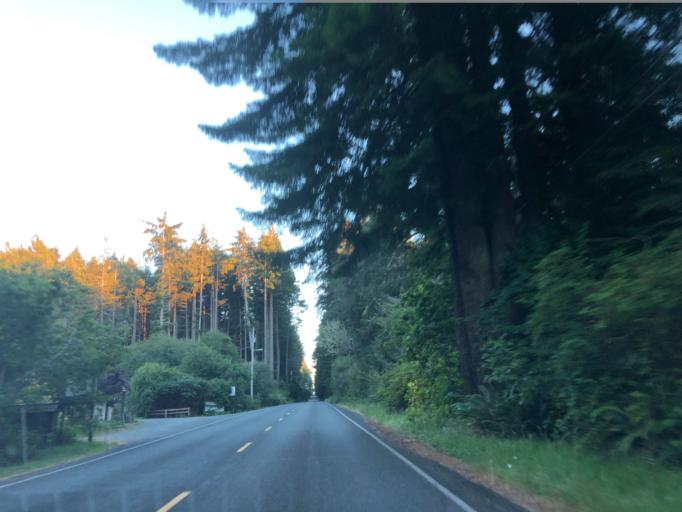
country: US
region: California
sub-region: Humboldt County
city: Westhaven-Moonstone
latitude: 41.0872
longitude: -124.1497
